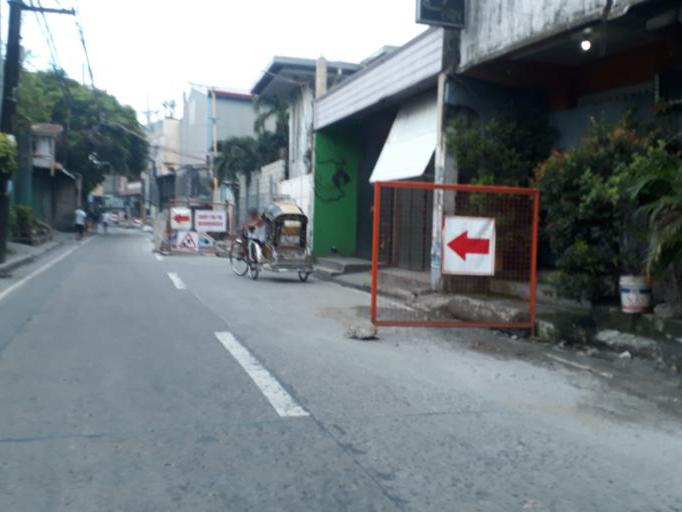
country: PH
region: Calabarzon
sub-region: Province of Rizal
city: Malabon
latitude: 14.6712
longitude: 120.9398
